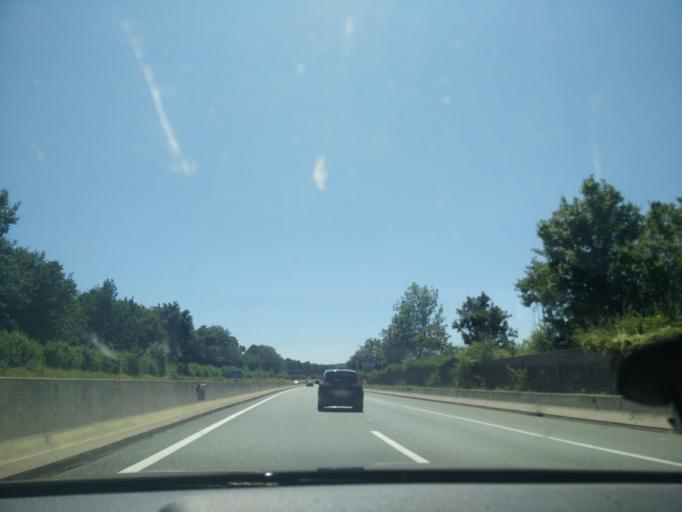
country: AT
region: Styria
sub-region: Politischer Bezirk Hartberg-Fuerstenfeld
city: Sebersdorf
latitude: 47.1899
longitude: 15.9959
